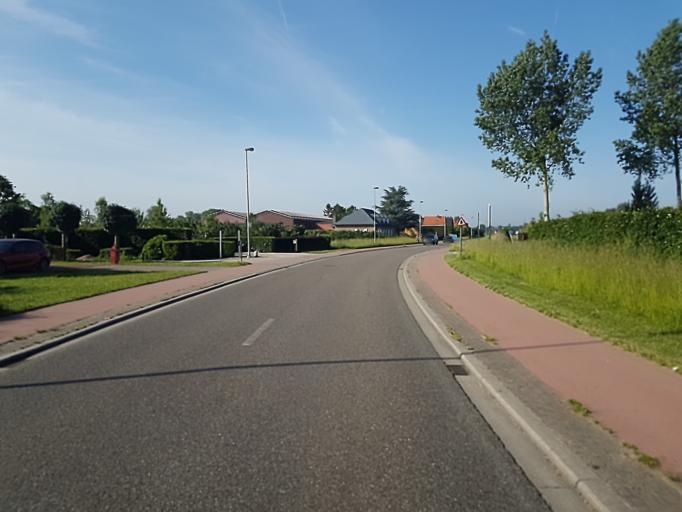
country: BE
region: Flanders
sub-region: Provincie Oost-Vlaanderen
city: Sint-Niklaas
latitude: 51.2045
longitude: 4.1915
